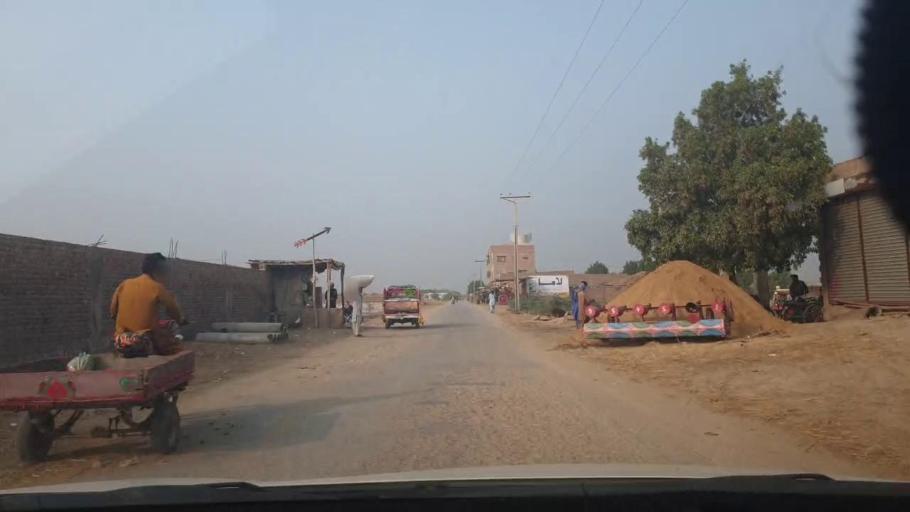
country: PK
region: Sindh
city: Bulri
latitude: 24.7583
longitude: 68.4194
